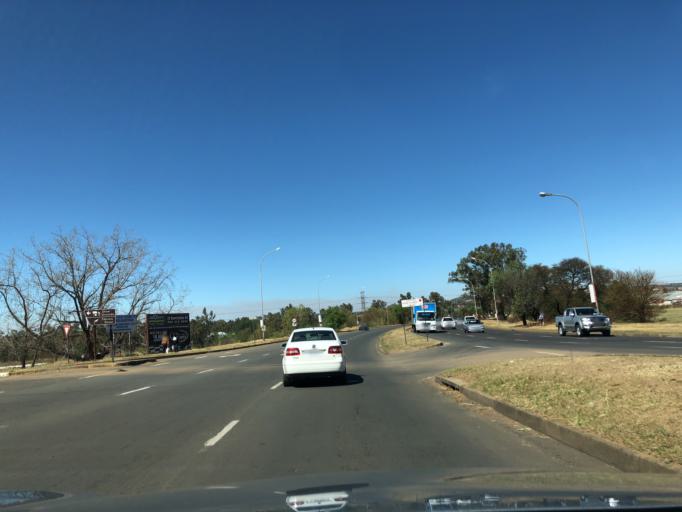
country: ZA
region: KwaZulu-Natal
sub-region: Amajuba District Municipality
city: Newcastle
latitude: -27.7435
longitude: 29.9370
